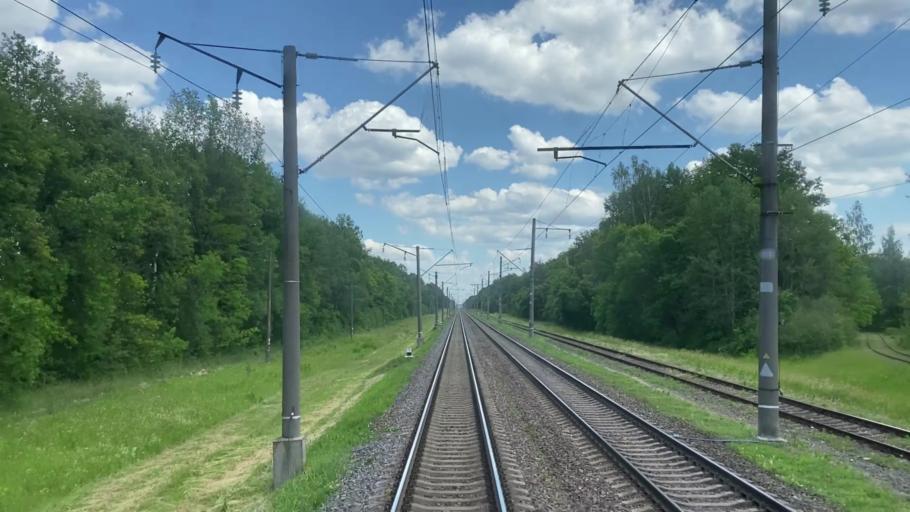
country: BY
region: Brest
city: Byaroza
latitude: 52.5401
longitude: 24.9345
